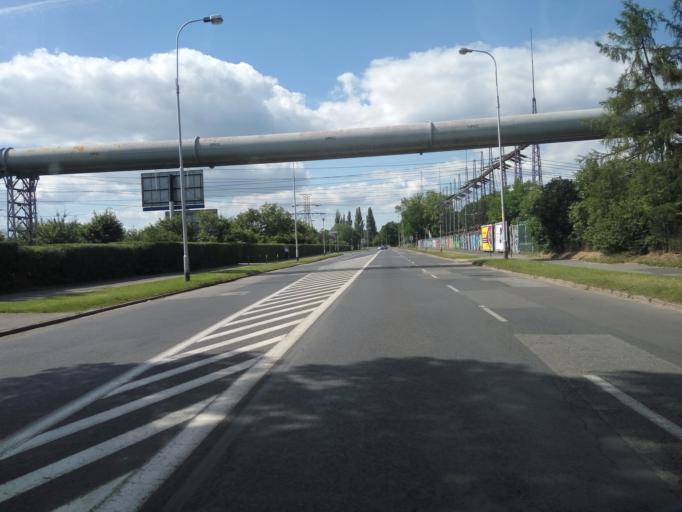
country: PL
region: Lower Silesian Voivodeship
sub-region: Powiat wroclawski
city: Wroclaw
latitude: 51.1224
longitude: 17.0121
